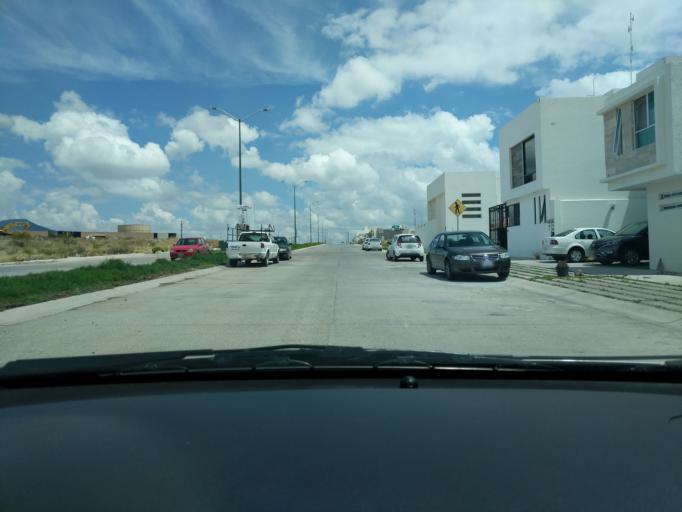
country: MX
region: San Luis Potosi
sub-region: Mexquitic de Carmona
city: Guadalupe Victoria
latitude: 22.1570
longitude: -101.0533
